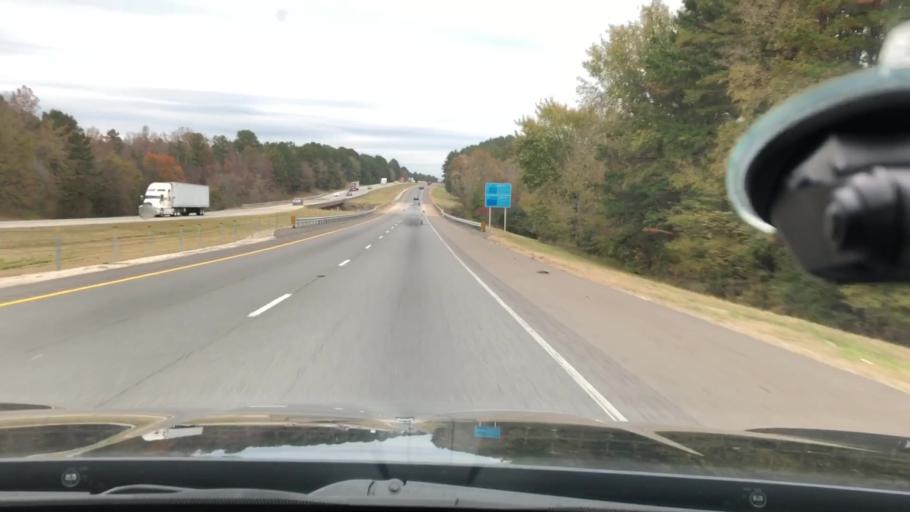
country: US
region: Arkansas
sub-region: Hot Spring County
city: Malvern
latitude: 34.3157
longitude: -92.9354
